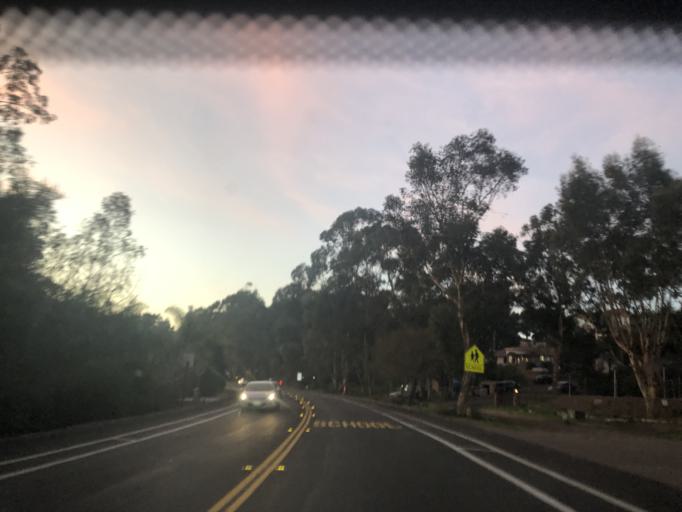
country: US
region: California
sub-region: San Diego County
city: Bonita
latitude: 32.6610
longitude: -117.0455
